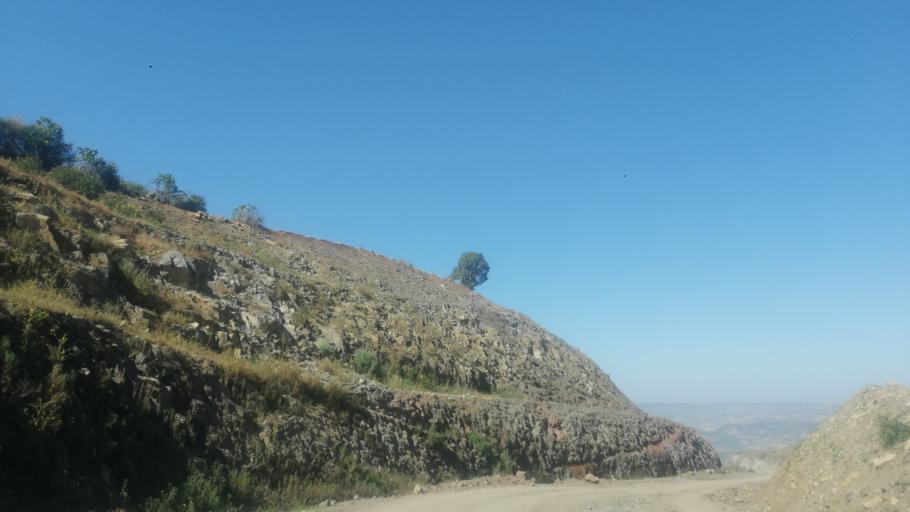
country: ET
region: Amhara
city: Addiet Canna
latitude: 11.1523
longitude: 37.8590
